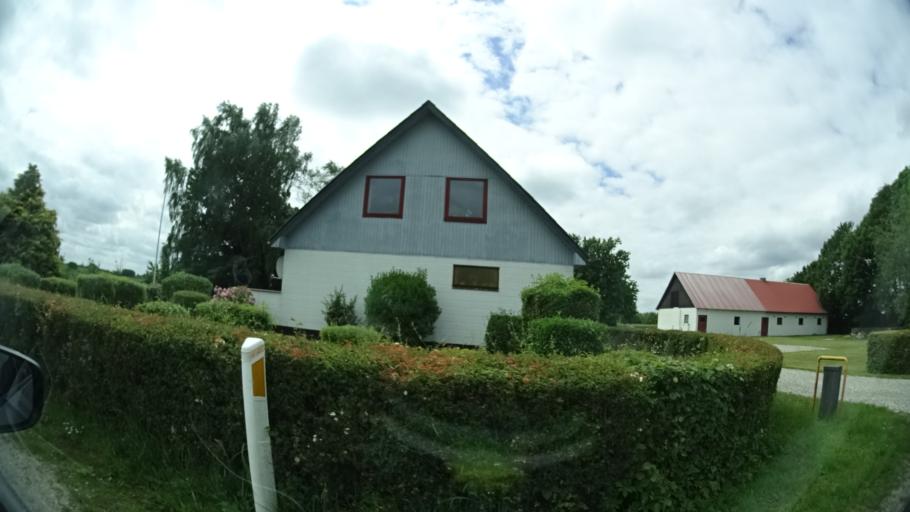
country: DK
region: Central Jutland
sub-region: Syddjurs Kommune
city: Ryomgard
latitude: 56.3942
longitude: 10.5634
